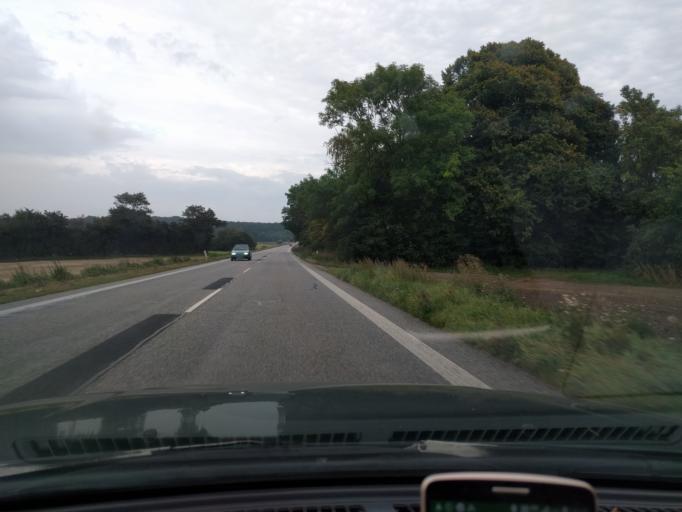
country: DK
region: Zealand
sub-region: Naestved Kommune
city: Naestved
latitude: 55.2060
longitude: 11.6593
